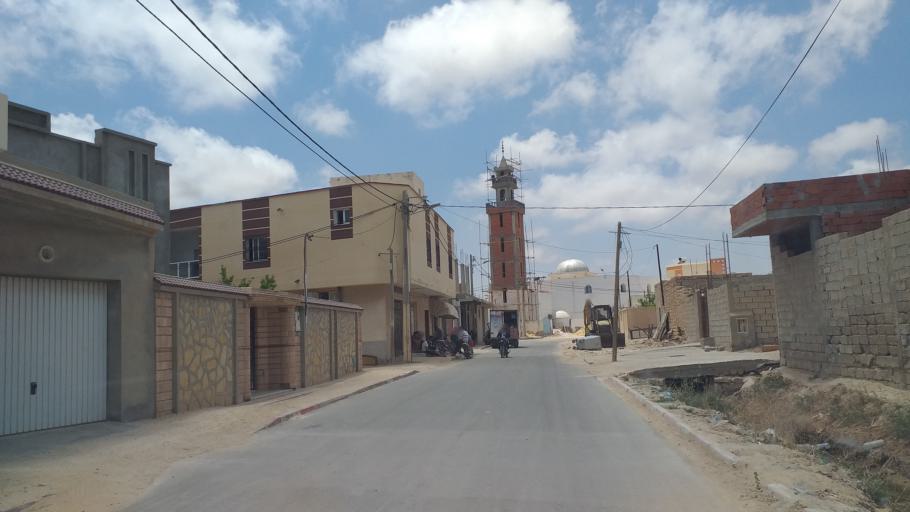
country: TN
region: Qabis
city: Gabes
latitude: 33.9340
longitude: 10.0609
